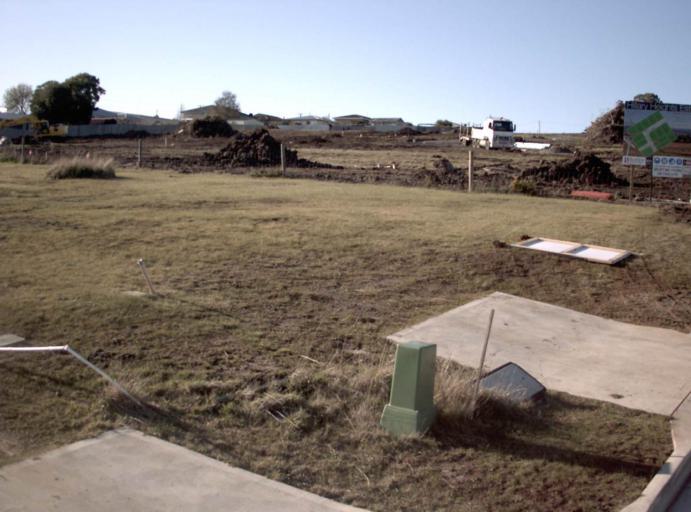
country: AU
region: Tasmania
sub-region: Launceston
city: Newstead
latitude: -41.4538
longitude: 147.2036
